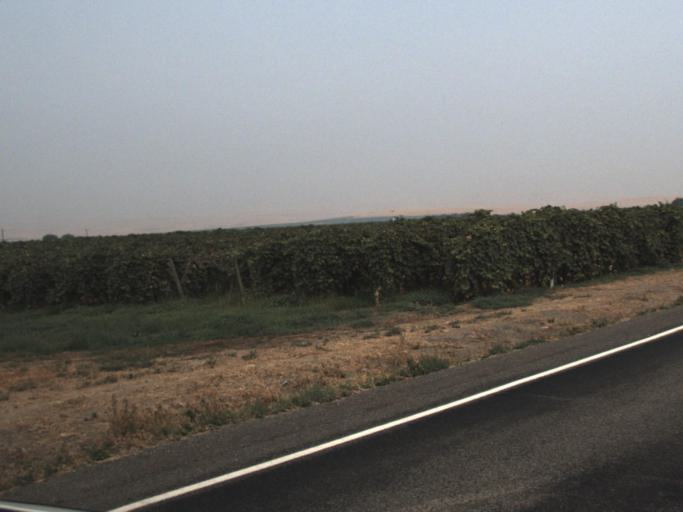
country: US
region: Washington
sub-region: Yakima County
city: Sunnyside
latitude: 46.3683
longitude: -119.9770
